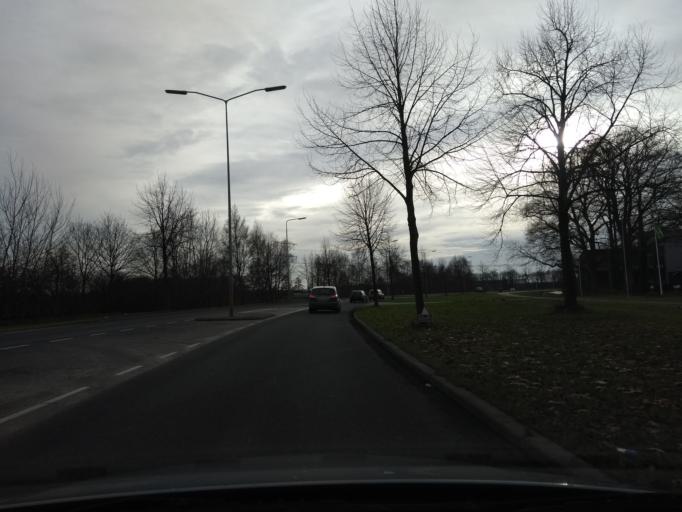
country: NL
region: Overijssel
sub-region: Gemeente Almelo
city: Almelo
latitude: 52.3276
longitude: 6.6542
